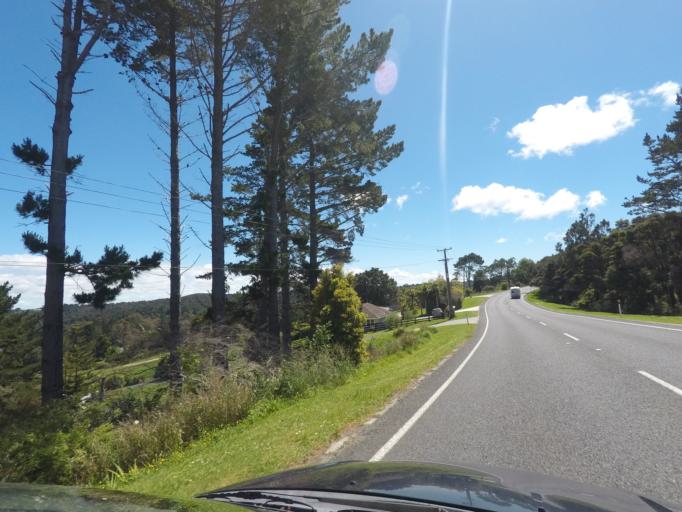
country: NZ
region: Auckland
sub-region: Auckland
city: Rothesay Bay
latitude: -36.7590
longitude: 174.6600
